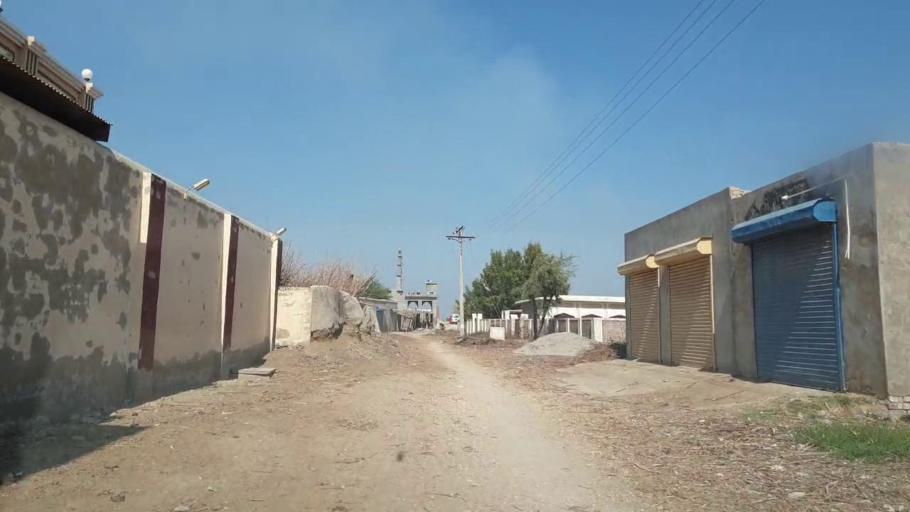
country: PK
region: Sindh
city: Mirpur Khas
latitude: 25.7364
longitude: 69.0972
